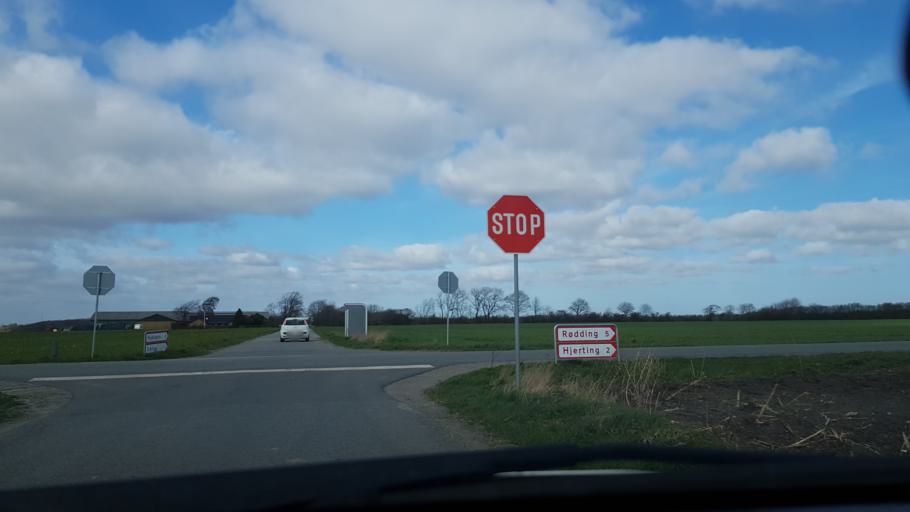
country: DK
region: South Denmark
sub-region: Vejen Kommune
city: Rodding
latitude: 55.3961
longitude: 9.0112
